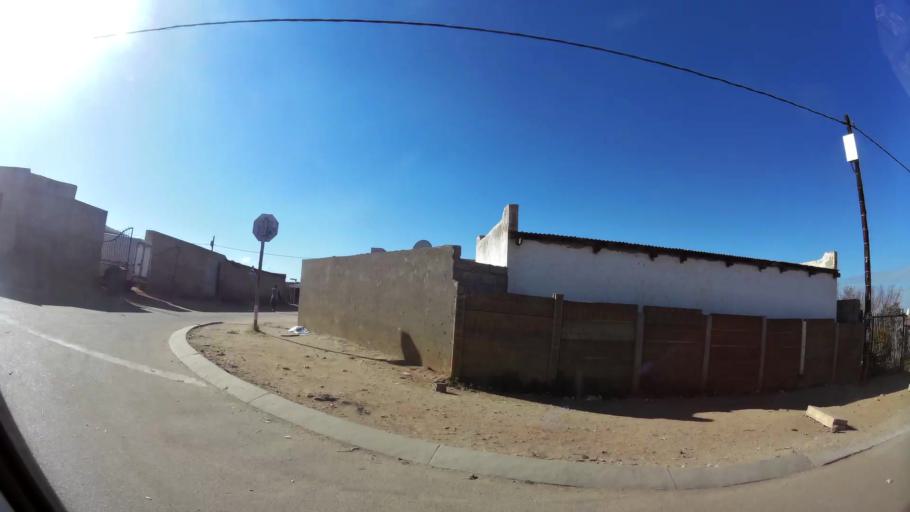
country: ZA
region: Gauteng
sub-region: City of Johannesburg Metropolitan Municipality
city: Diepsloot
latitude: -25.9076
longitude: 28.0928
